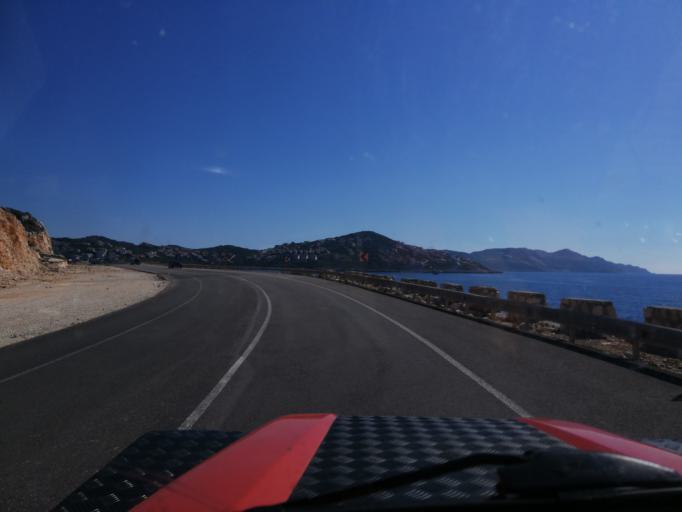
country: TR
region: Antalya
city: Kas
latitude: 36.2027
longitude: 29.5839
